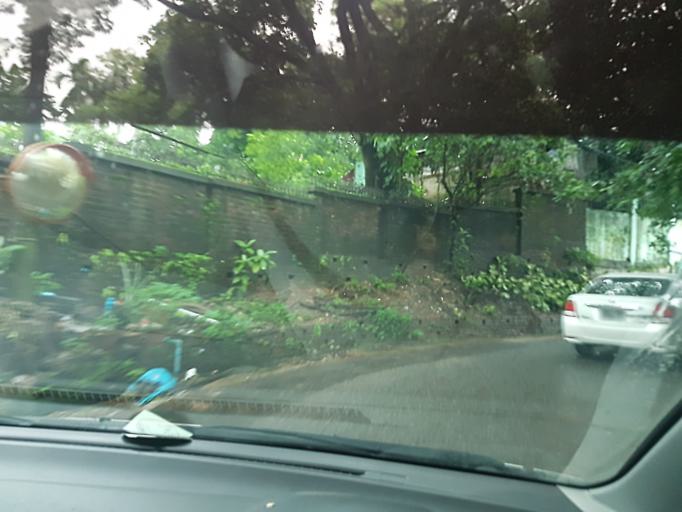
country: MM
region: Yangon
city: Yangon
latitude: 16.8136
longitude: 96.1546
